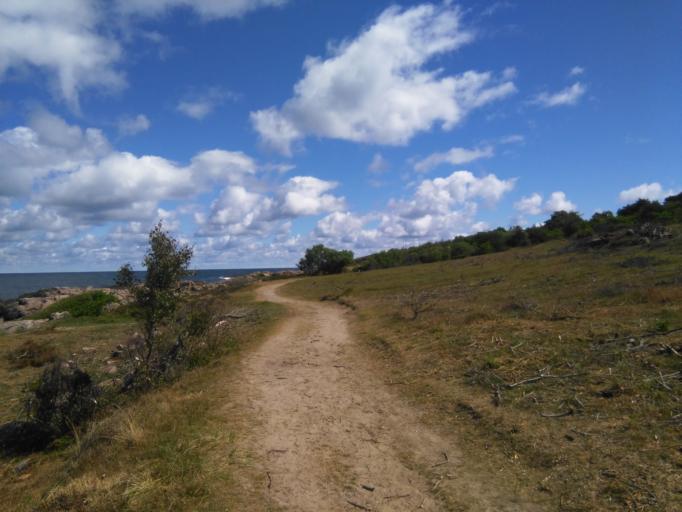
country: DK
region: Capital Region
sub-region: Bornholm Kommune
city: Ronne
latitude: 55.2959
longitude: 14.7666
